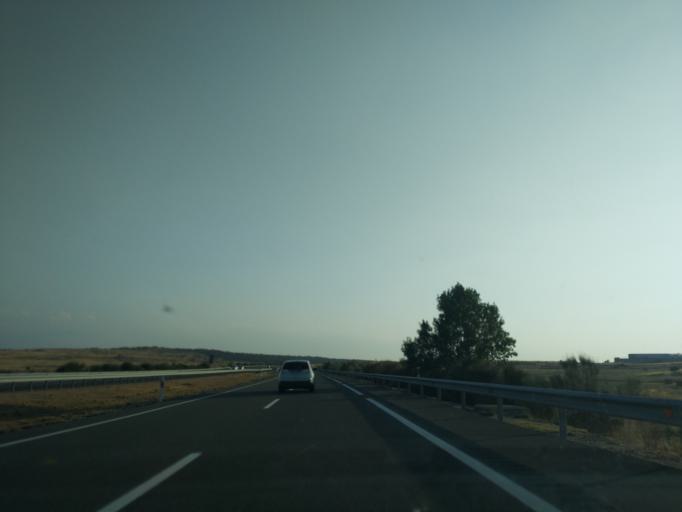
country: ES
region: Castille and Leon
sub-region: Provincia de Avila
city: Berrocalejo de Aragona
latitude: 40.6821
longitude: -4.6017
